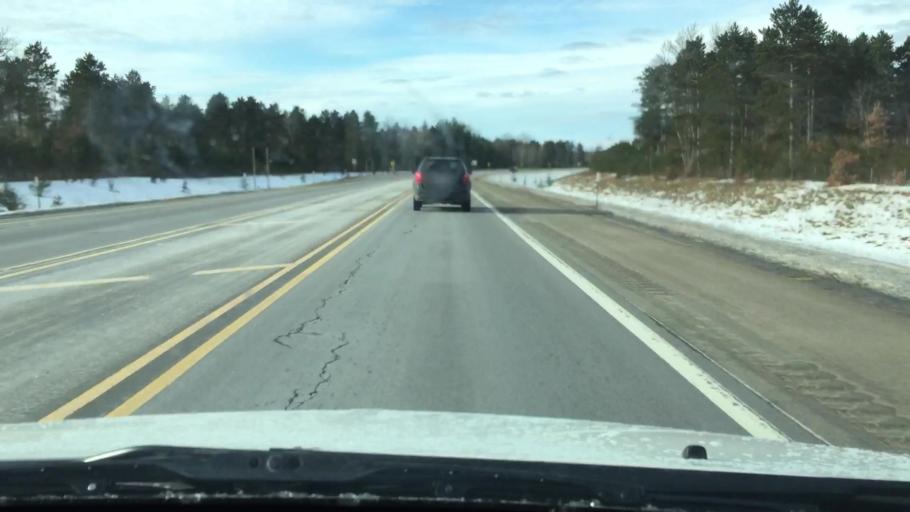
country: US
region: Michigan
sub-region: Wexford County
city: Manton
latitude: 44.4689
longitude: -85.4020
